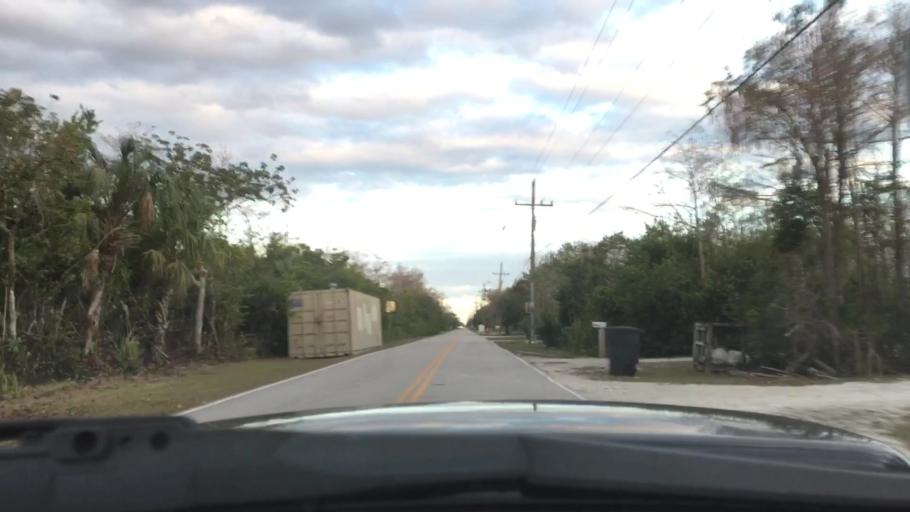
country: US
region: Florida
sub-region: Miami-Dade County
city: Kendall West
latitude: 25.7607
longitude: -80.8486
